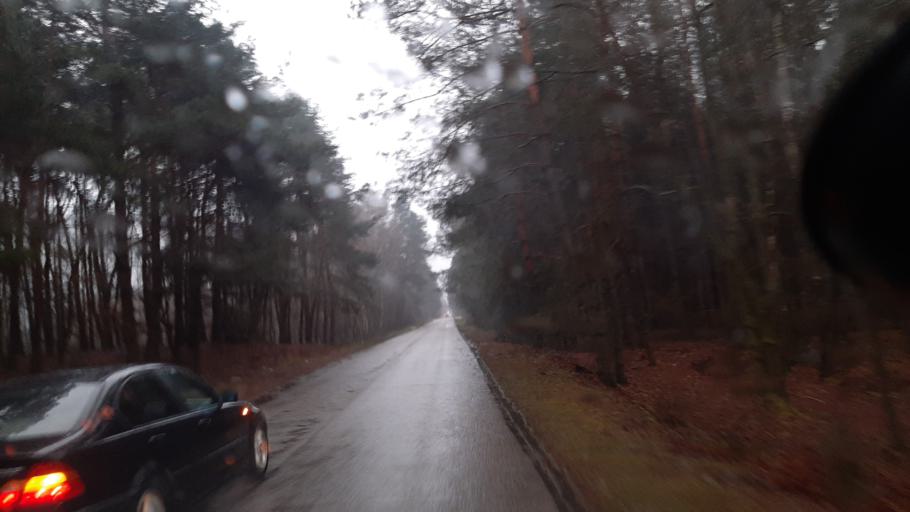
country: PL
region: Lublin Voivodeship
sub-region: Powiat lubartowski
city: Kamionka
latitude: 51.5086
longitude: 22.4901
